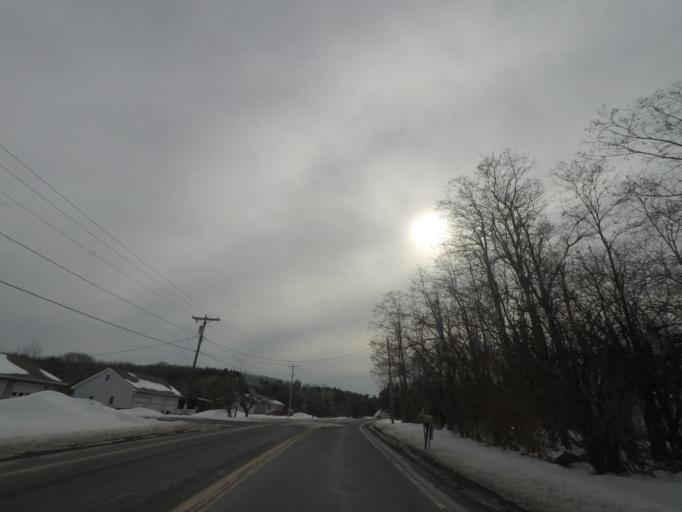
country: US
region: New York
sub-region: Albany County
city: Altamont
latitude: 42.6865
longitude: -74.0703
